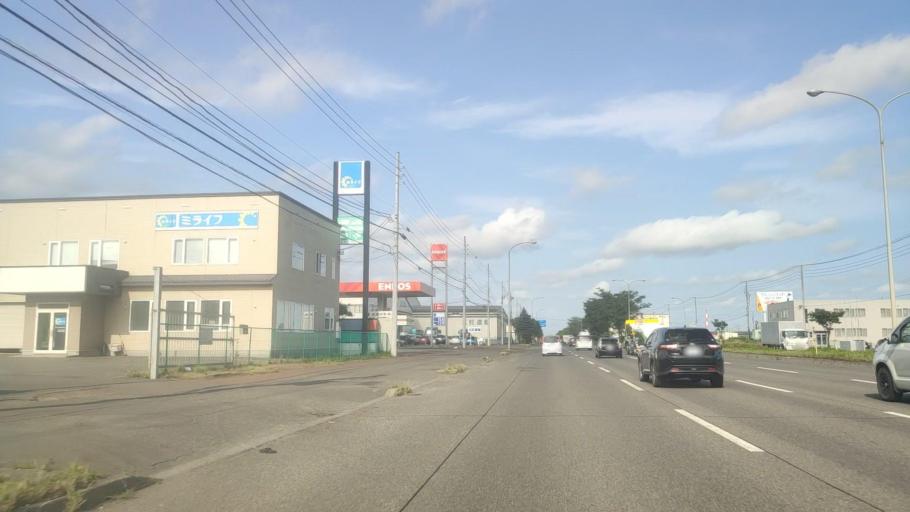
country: JP
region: Hokkaido
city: Tomakomai
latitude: 42.6546
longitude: 141.6495
